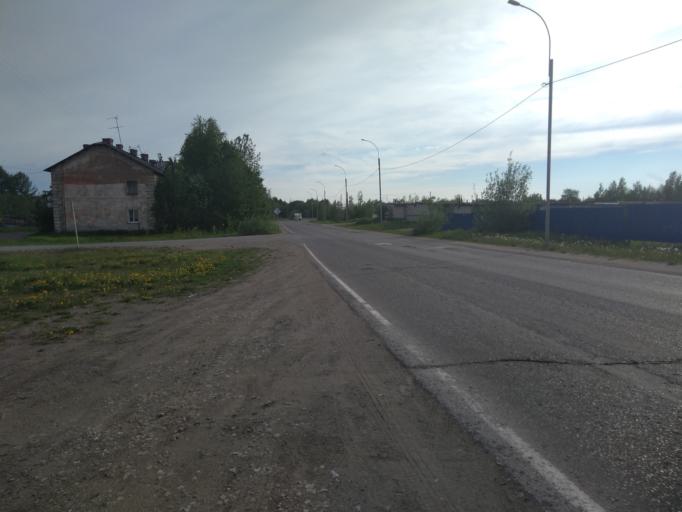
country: RU
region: Komi Republic
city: Pechora
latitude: 65.1469
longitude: 57.2102
